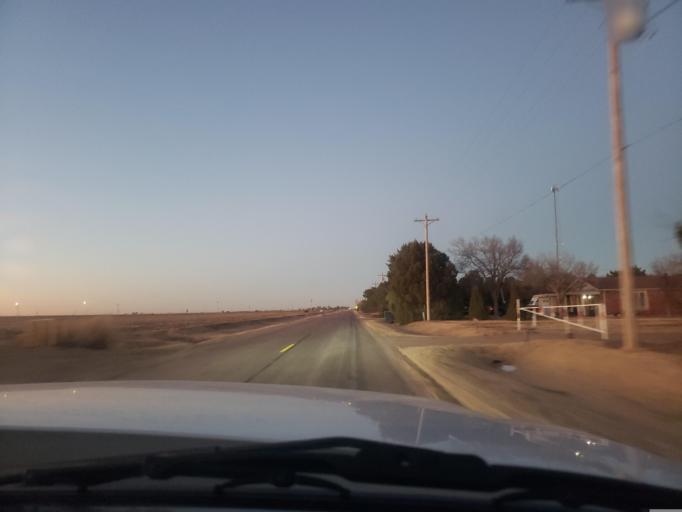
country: US
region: Kansas
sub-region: Finney County
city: Garden City
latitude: 37.9970
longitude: -100.8749
